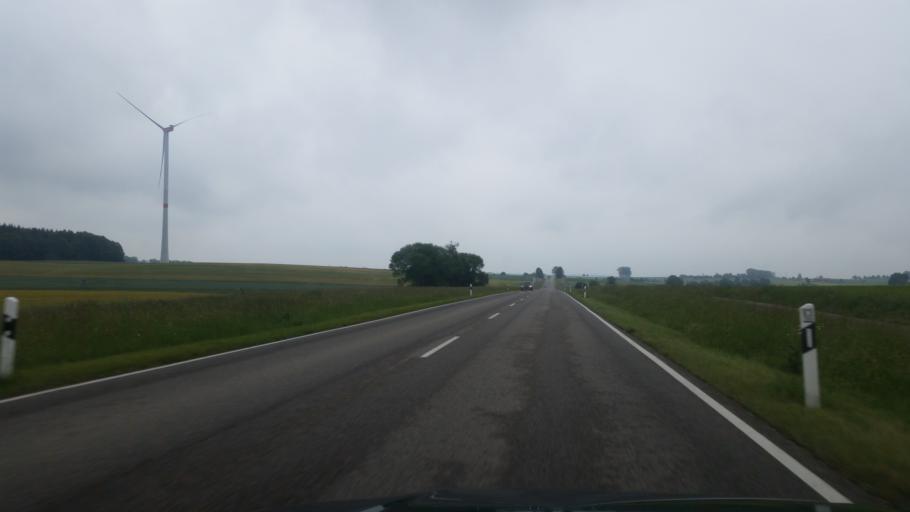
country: DE
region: Baden-Wuerttemberg
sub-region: Regierungsbezirk Stuttgart
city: Stodtlen
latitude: 48.9344
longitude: 10.2819
